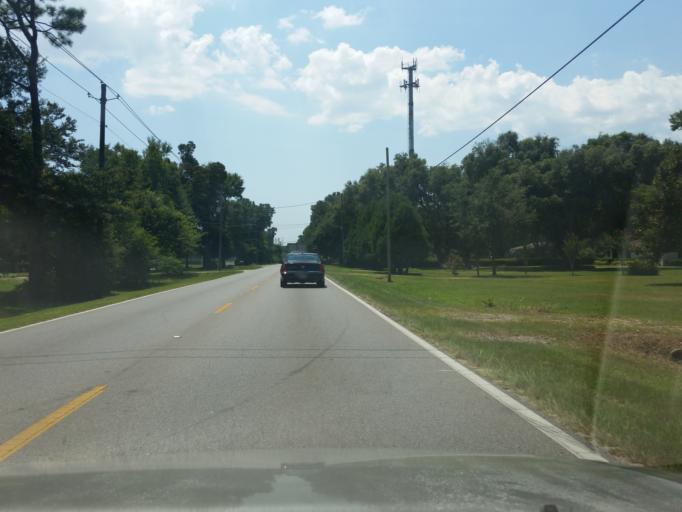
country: US
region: Florida
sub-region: Escambia County
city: Ensley
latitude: 30.5455
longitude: -87.2802
